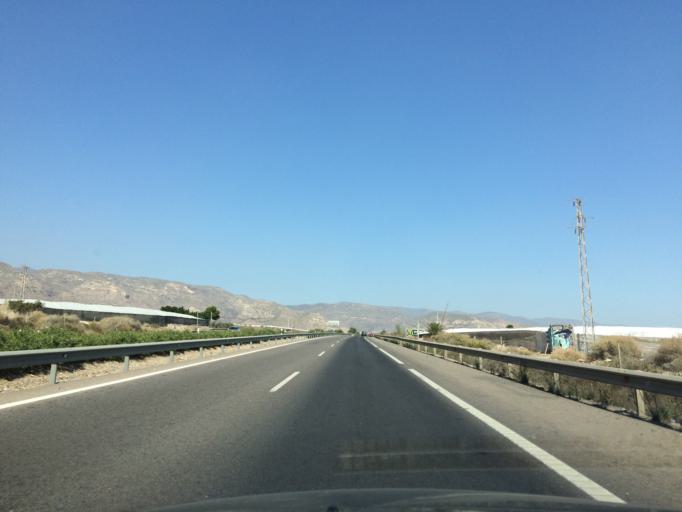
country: ES
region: Andalusia
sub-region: Provincia de Almeria
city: Vicar
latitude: 36.8015
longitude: -2.6774
